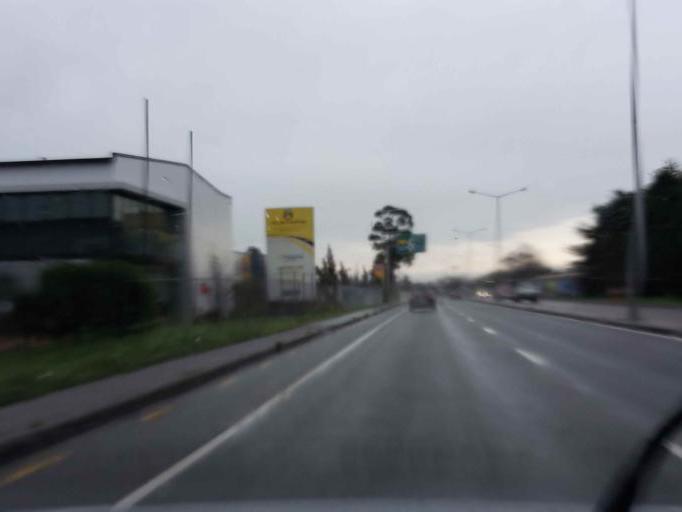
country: NZ
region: Canterbury
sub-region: Selwyn District
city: Prebbleton
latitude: -43.5392
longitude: 172.5578
